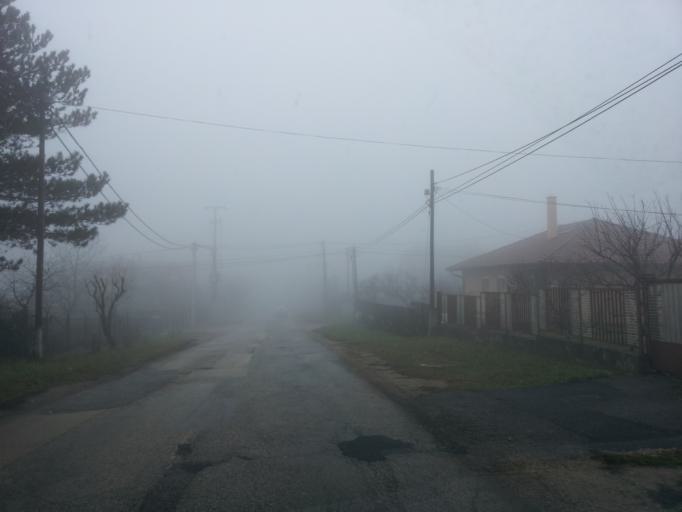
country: HU
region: Pest
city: Toeroekbalint
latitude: 47.4220
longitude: 18.8824
